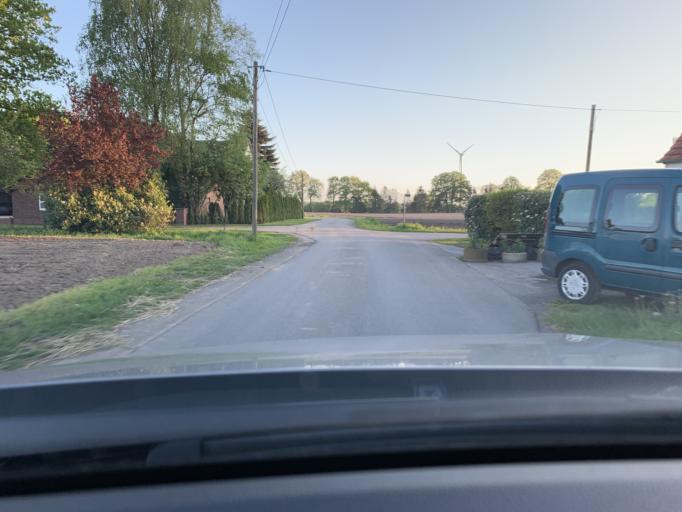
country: DE
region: North Rhine-Westphalia
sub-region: Regierungsbezirk Detmold
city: Langenberg
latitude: 51.8255
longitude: 8.3643
